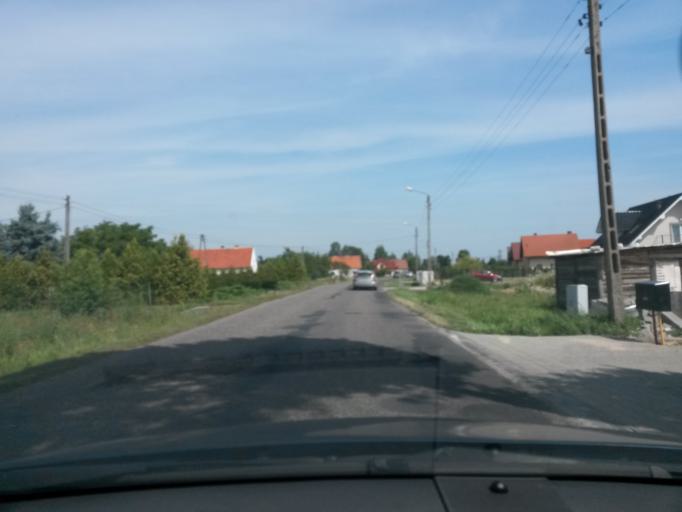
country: PL
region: Lower Silesian Voivodeship
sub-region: Powiat legnicki
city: Prochowice
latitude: 51.2590
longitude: 16.3644
